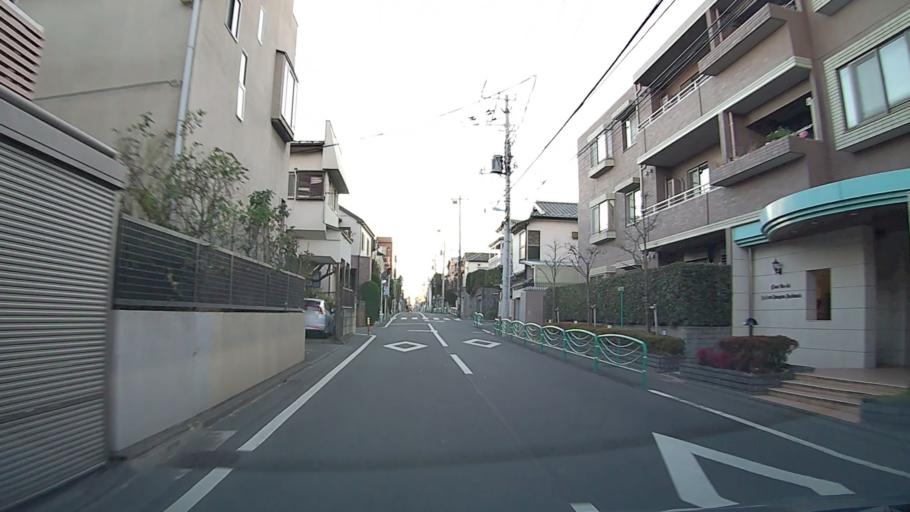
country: JP
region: Tokyo
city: Musashino
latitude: 35.7172
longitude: 139.6110
